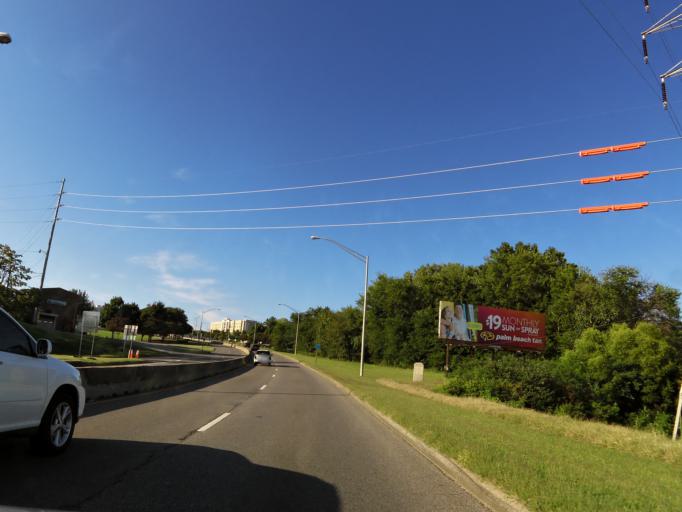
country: US
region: Alabama
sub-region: Lauderdale County
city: Florence
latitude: 34.7923
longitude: -87.6726
